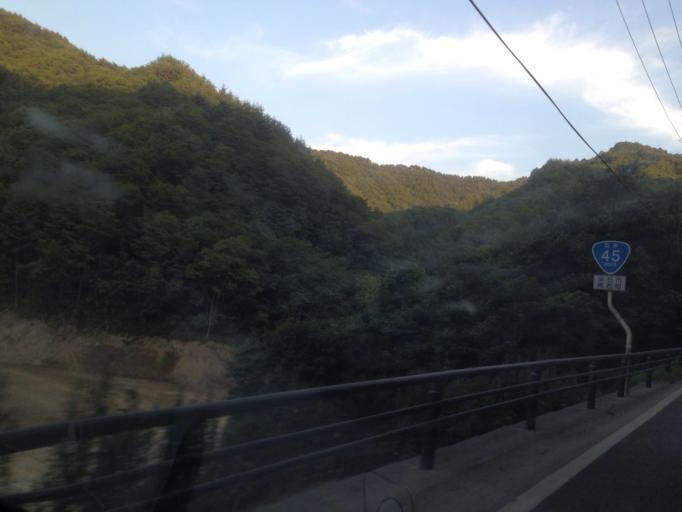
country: JP
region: Iwate
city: Kamaishi
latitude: 39.2973
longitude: 141.8836
